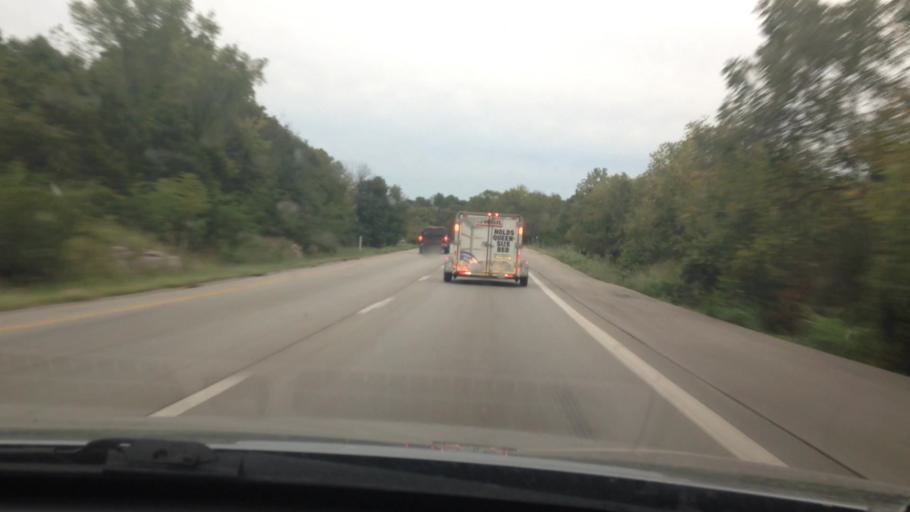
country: US
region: Missouri
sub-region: Jackson County
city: Raytown
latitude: 38.9697
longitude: -94.4405
